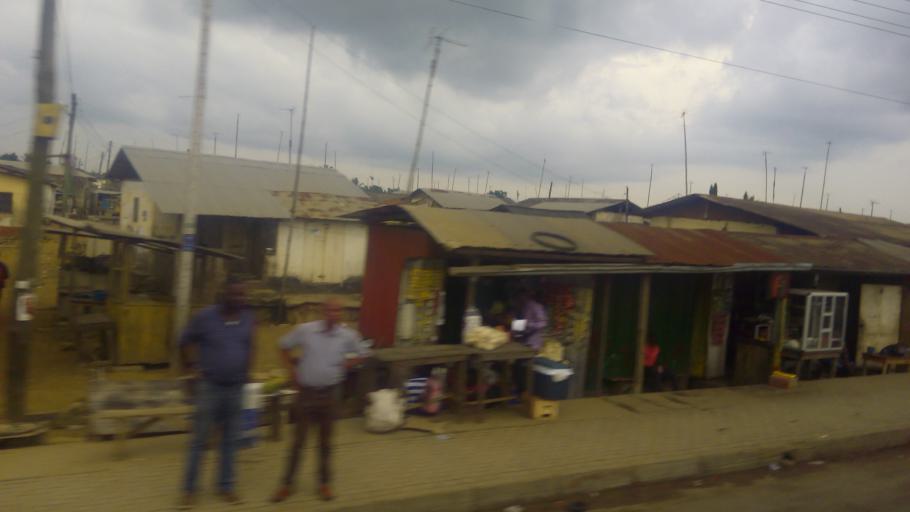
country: GH
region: Western
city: Takoradi
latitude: 4.8945
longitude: -1.9393
